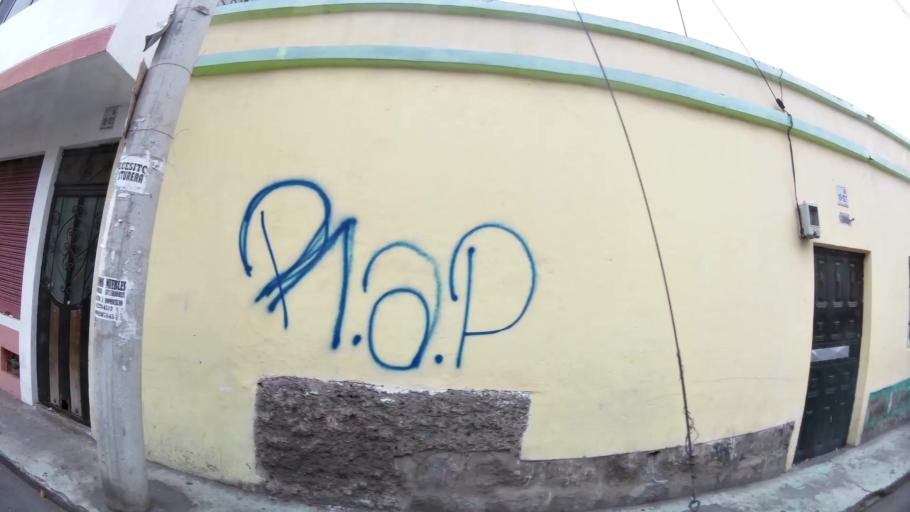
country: EC
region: Cotopaxi
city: Latacunga
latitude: -0.9304
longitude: -78.6114
